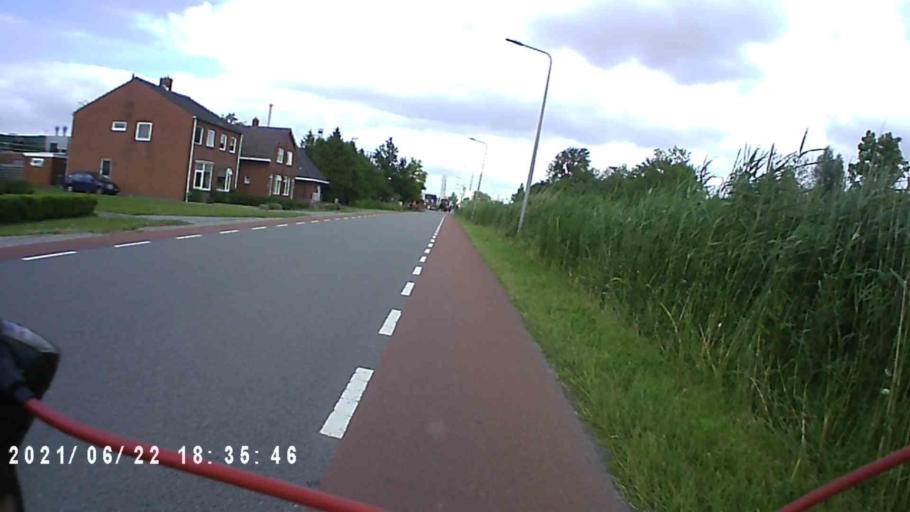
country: NL
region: Groningen
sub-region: Gemeente Zuidhorn
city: Aduard
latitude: 53.2107
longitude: 6.4804
